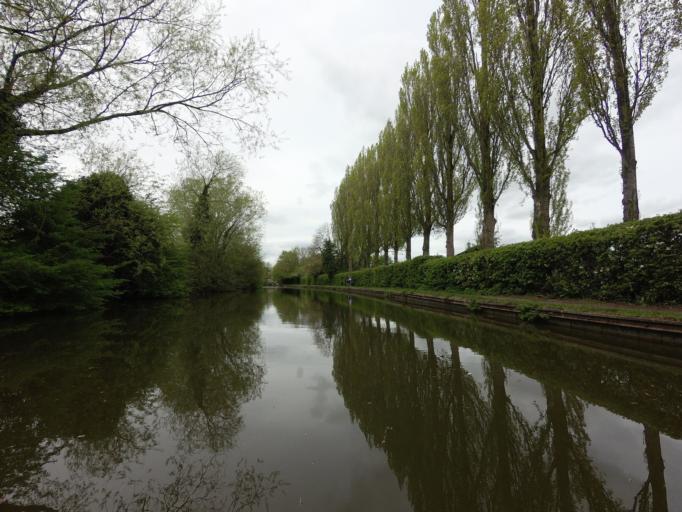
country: GB
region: England
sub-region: Milton Keynes
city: Simpson
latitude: 52.0215
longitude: -0.7203
